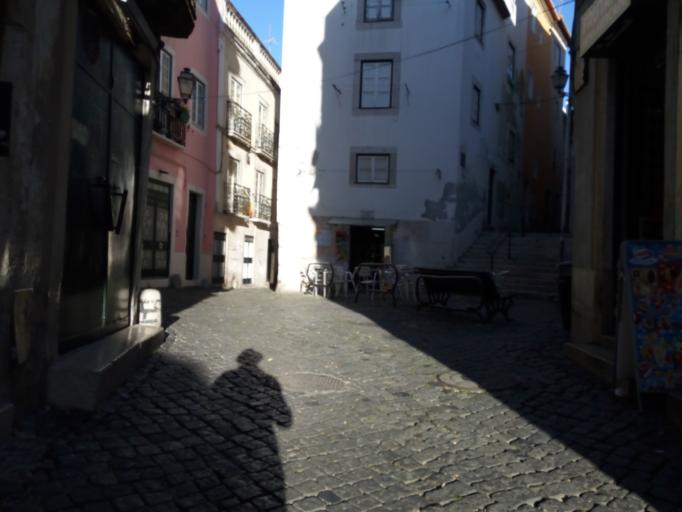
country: PT
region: Lisbon
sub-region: Lisbon
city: Lisbon
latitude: 38.7126
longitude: -9.1277
